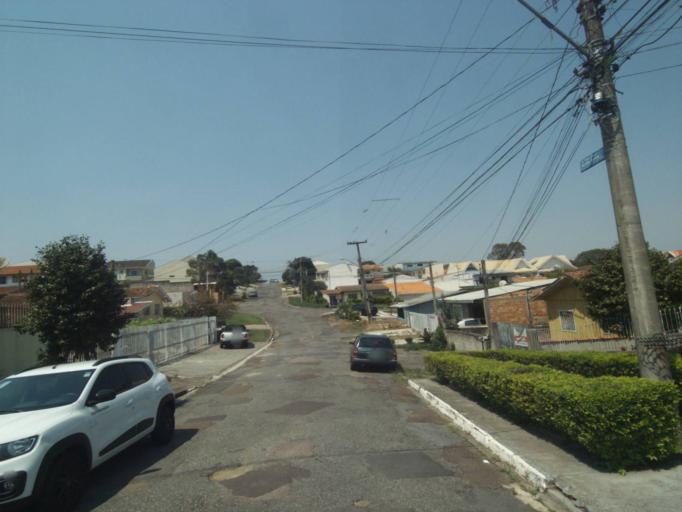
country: BR
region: Parana
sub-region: Sao Jose Dos Pinhais
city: Sao Jose dos Pinhais
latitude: -25.5058
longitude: -49.2668
